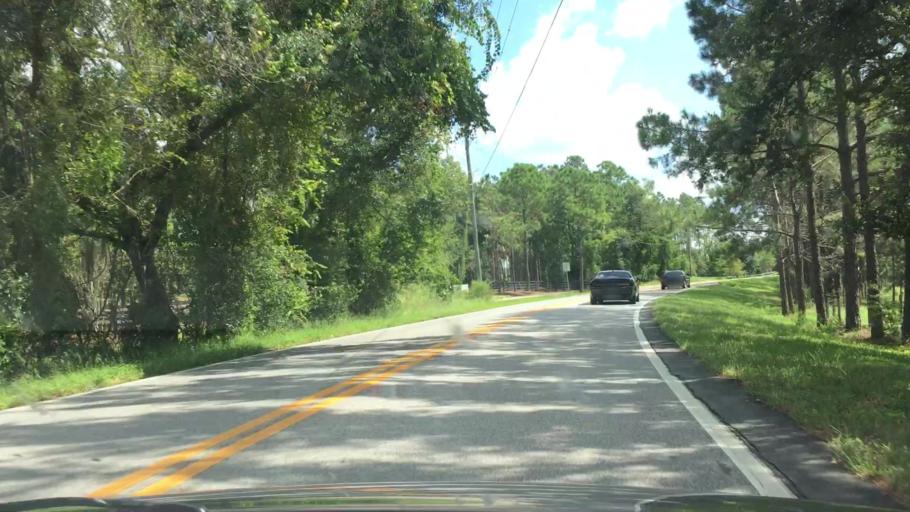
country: US
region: Florida
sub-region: Lake County
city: Minneola
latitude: 28.5692
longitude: -81.7091
